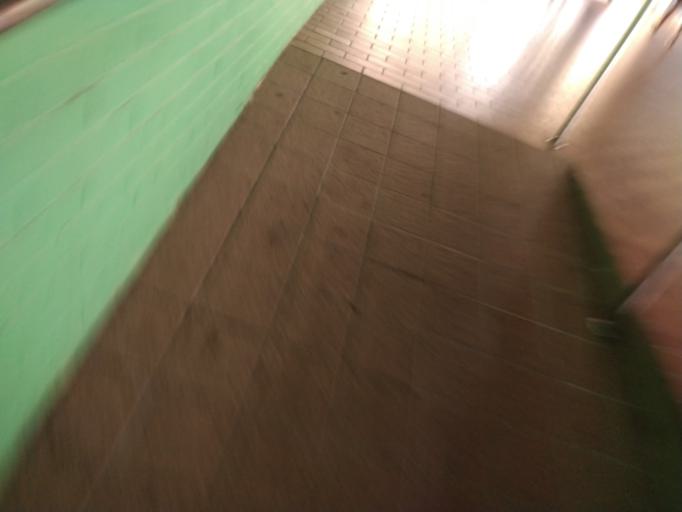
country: SG
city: Singapore
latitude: 1.2890
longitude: 103.8202
